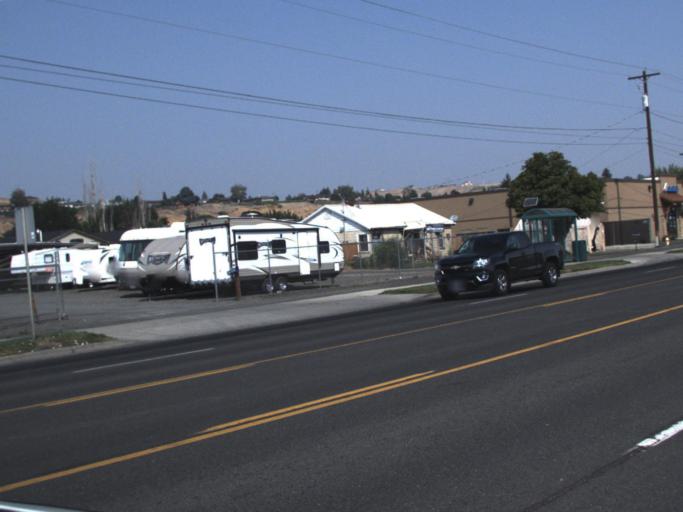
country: US
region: Washington
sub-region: Yakima County
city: Selah
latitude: 46.6454
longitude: -120.5302
